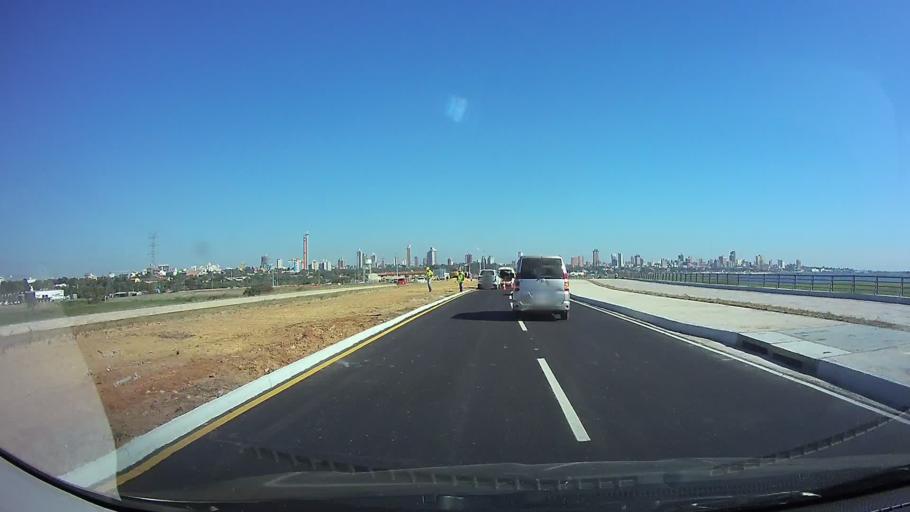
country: PY
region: Asuncion
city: Asuncion
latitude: -25.2674
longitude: -57.6110
